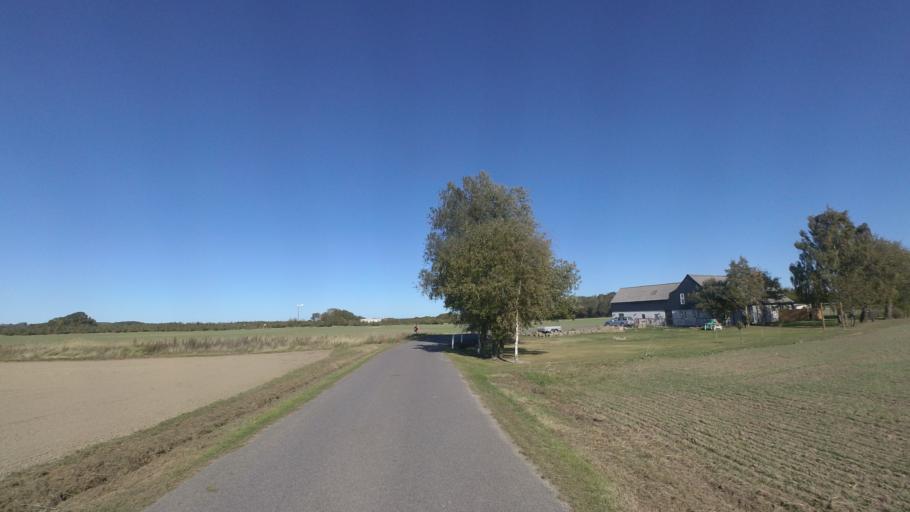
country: DK
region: Capital Region
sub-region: Bornholm Kommune
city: Nexo
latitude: 55.1205
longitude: 15.0482
